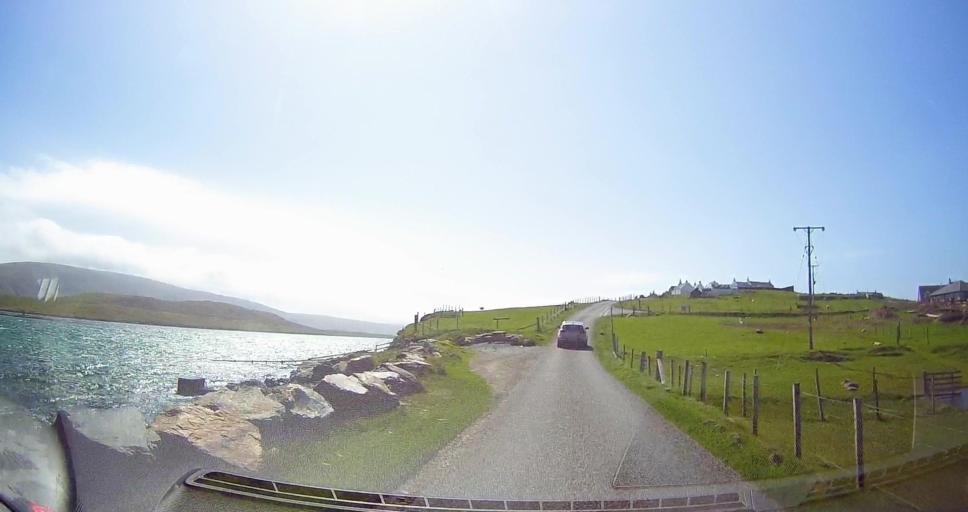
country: GB
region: Scotland
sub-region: Shetland Islands
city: Sandwick
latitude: 60.0643
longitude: -1.3398
